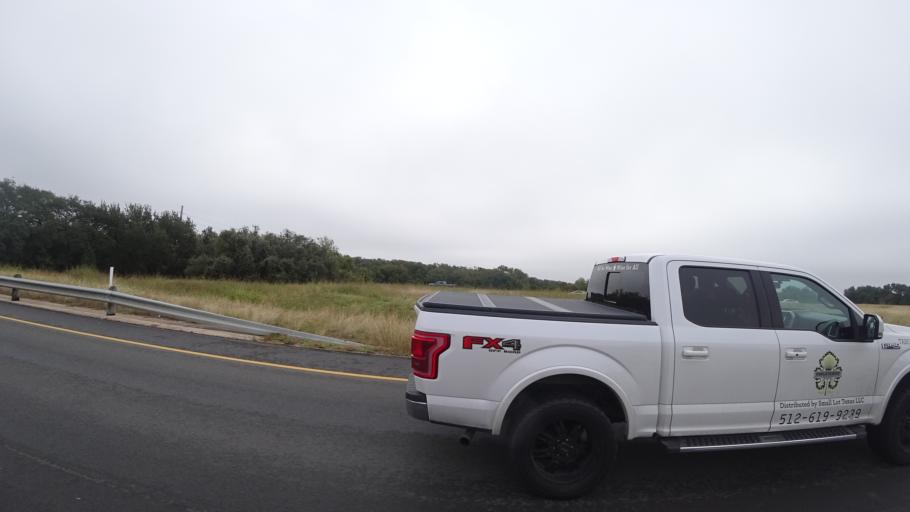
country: US
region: Texas
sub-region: Travis County
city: Shady Hollow
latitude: 30.1985
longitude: -97.8681
